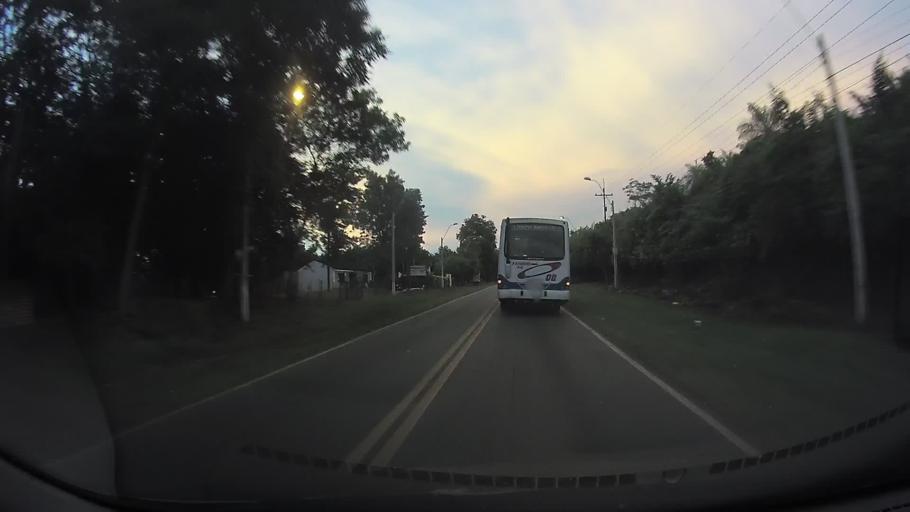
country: PY
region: Central
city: Ita
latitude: -25.4734
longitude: -57.3635
